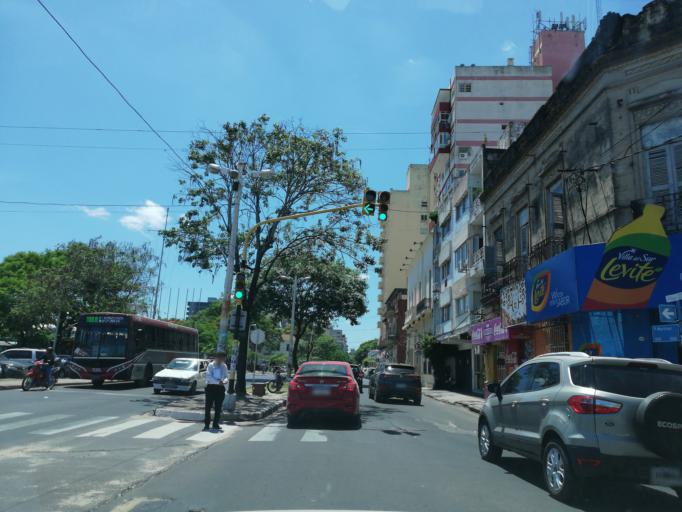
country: AR
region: Corrientes
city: Corrientes
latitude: -27.4618
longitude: -58.8376
